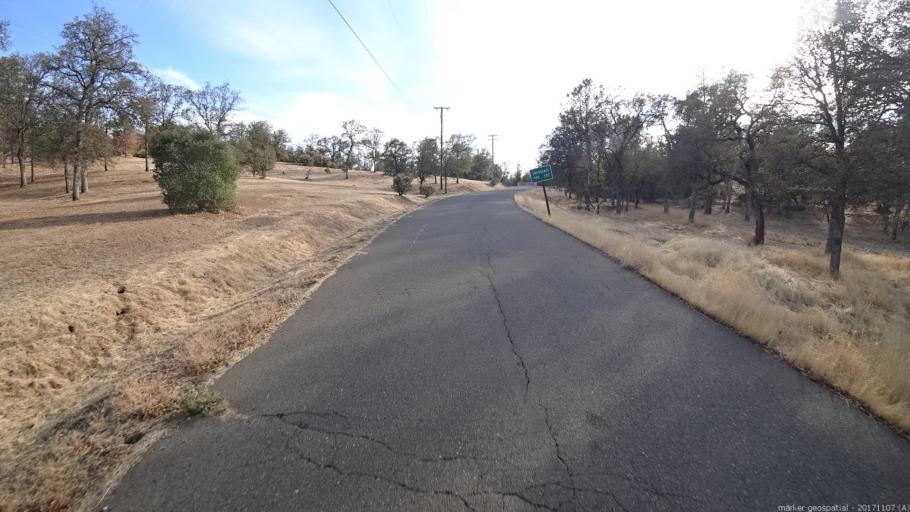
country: US
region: California
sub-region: Shasta County
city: Shasta
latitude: 40.5160
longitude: -122.4598
